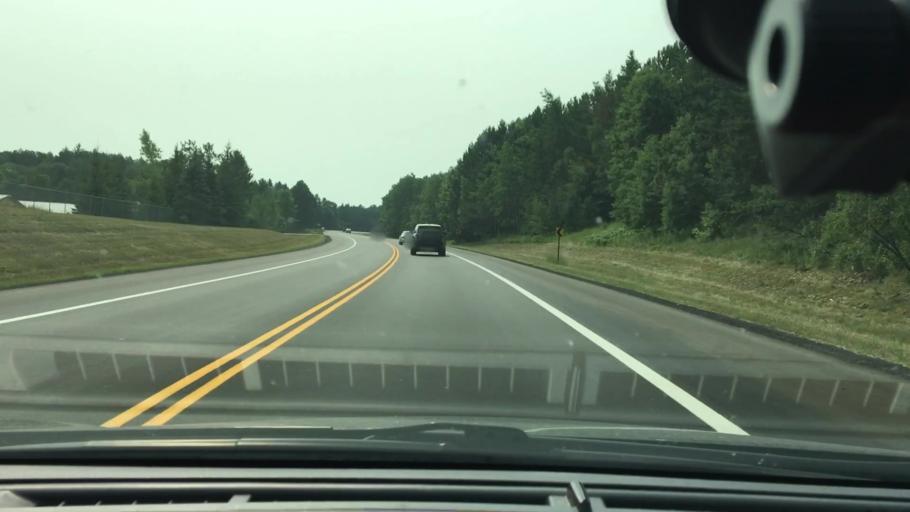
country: US
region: Minnesota
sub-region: Crow Wing County
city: Brainerd
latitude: 46.4166
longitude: -94.1784
